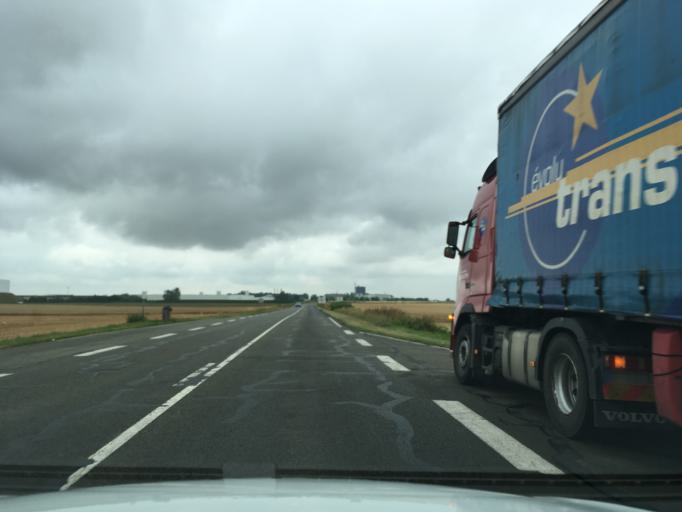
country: FR
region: Picardie
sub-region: Departement de la Somme
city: Roisel
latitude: 49.8784
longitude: 3.0600
